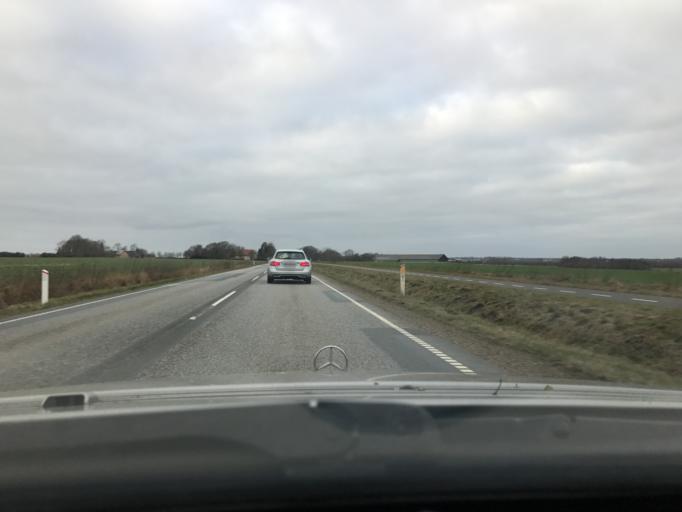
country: DK
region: South Denmark
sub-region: Tonder Kommune
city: Toftlund
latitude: 55.1523
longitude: 9.1008
